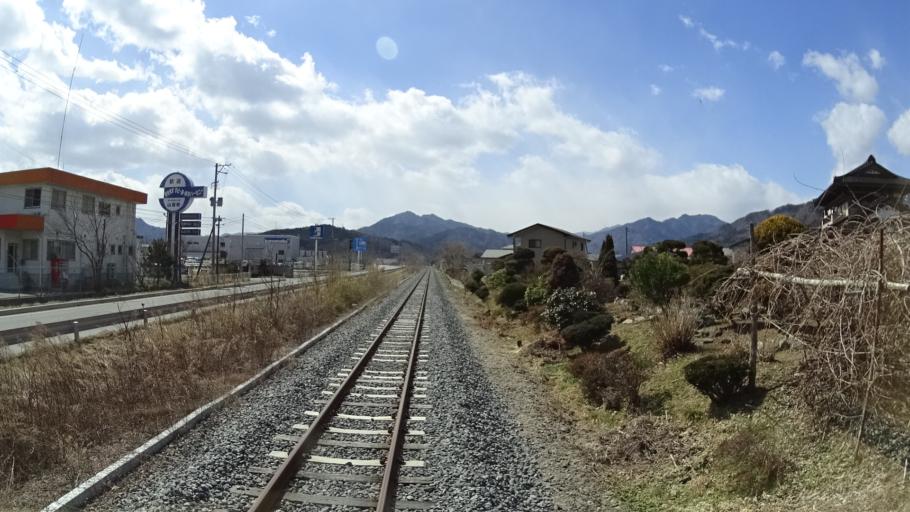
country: JP
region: Iwate
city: Yamada
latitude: 39.5424
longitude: 141.9308
